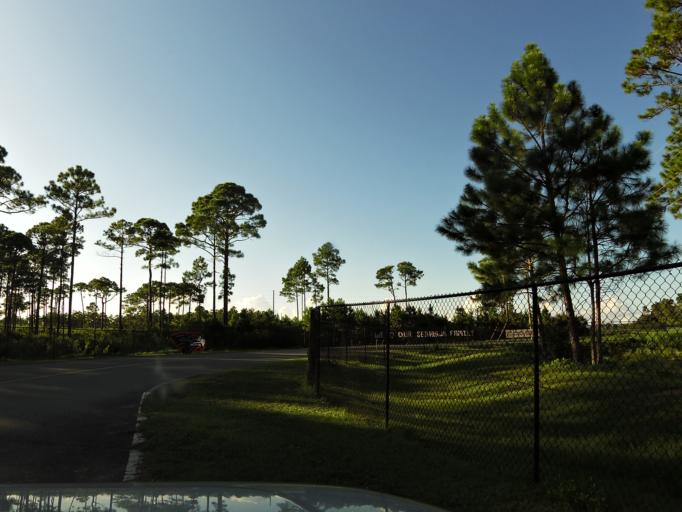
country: US
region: Florida
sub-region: Franklin County
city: Eastpoint
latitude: 29.7629
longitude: -84.8161
